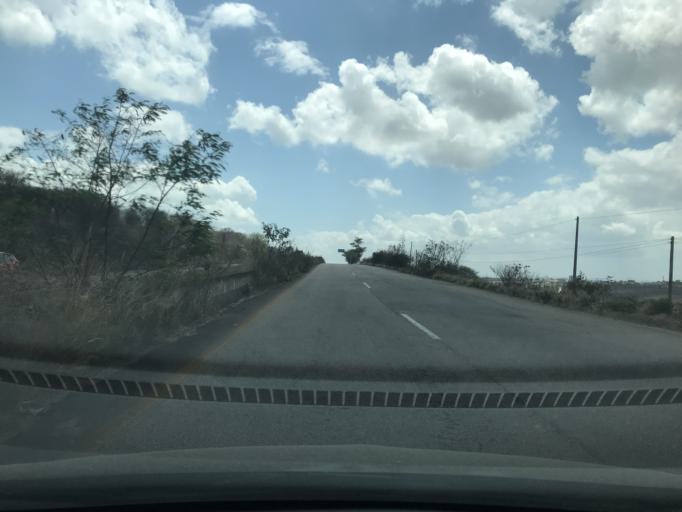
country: BR
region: Pernambuco
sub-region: Caruaru
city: Caruaru
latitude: -8.3061
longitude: -35.9368
